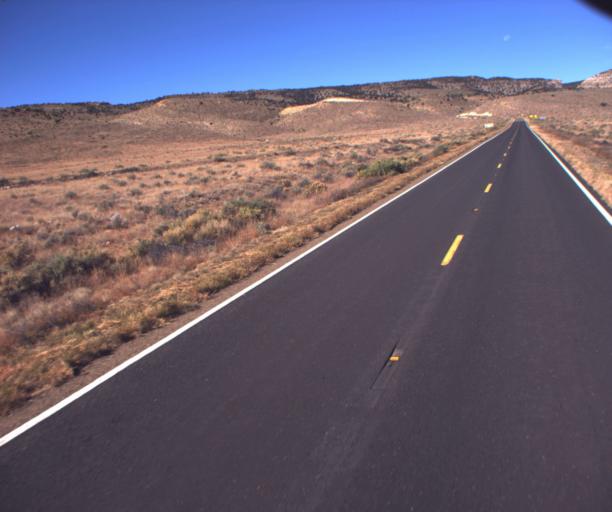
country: US
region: Arizona
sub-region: Coconino County
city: Fredonia
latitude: 36.7321
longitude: -112.0497
